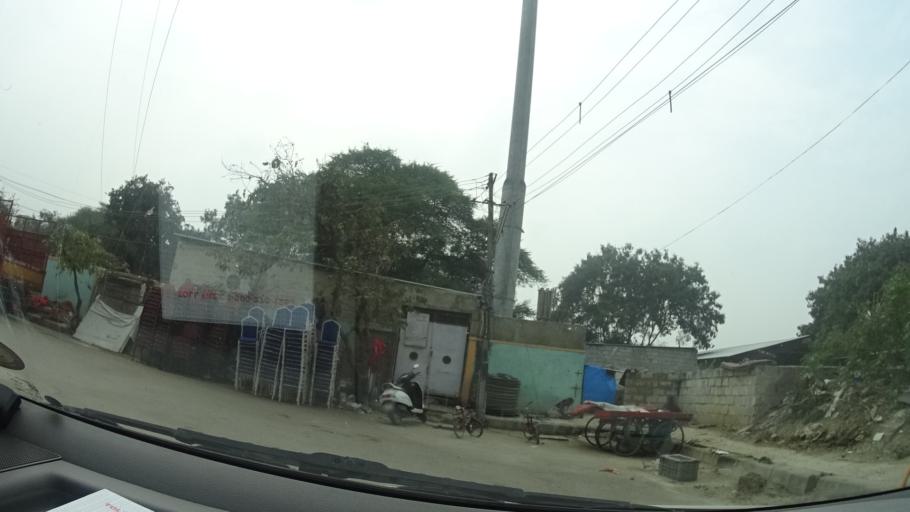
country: IN
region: Karnataka
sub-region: Bangalore Urban
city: Bangalore
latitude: 13.0284
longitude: 77.6240
